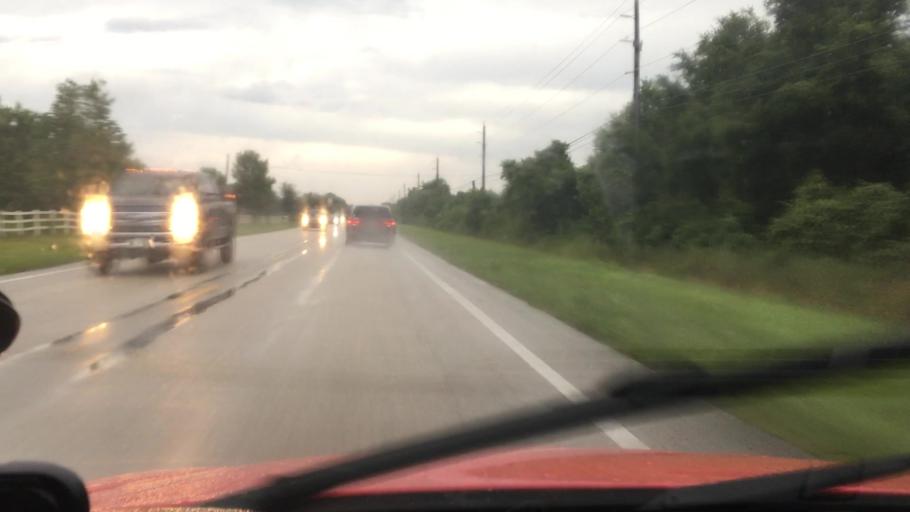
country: US
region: Florida
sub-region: Volusia County
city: Samsula-Spruce Creek
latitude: 29.0771
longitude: -81.0682
